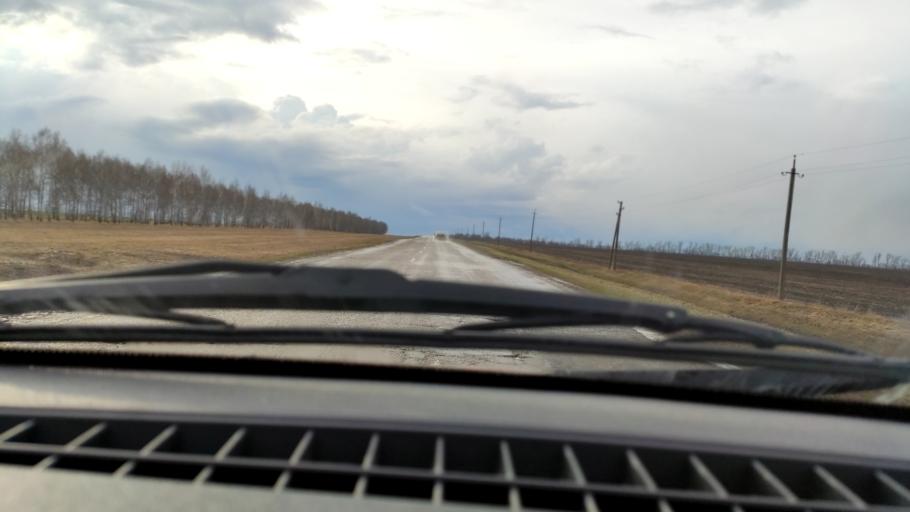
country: RU
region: Bashkortostan
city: Kushnarenkovo
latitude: 55.0999
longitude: 55.0438
